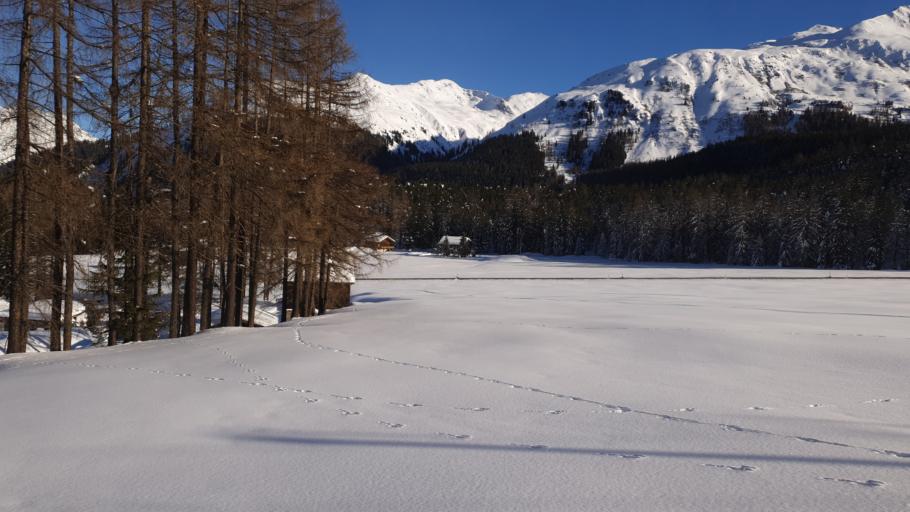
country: CH
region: Grisons
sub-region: Praettigau/Davos District
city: Davos
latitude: 46.8394
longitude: 9.8552
